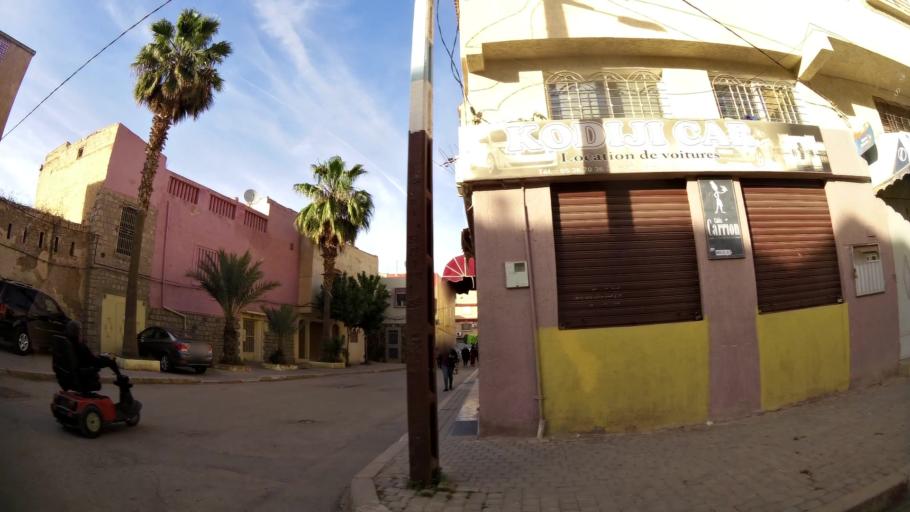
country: MA
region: Oriental
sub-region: Oujda-Angad
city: Oujda
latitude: 34.6782
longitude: -1.9137
